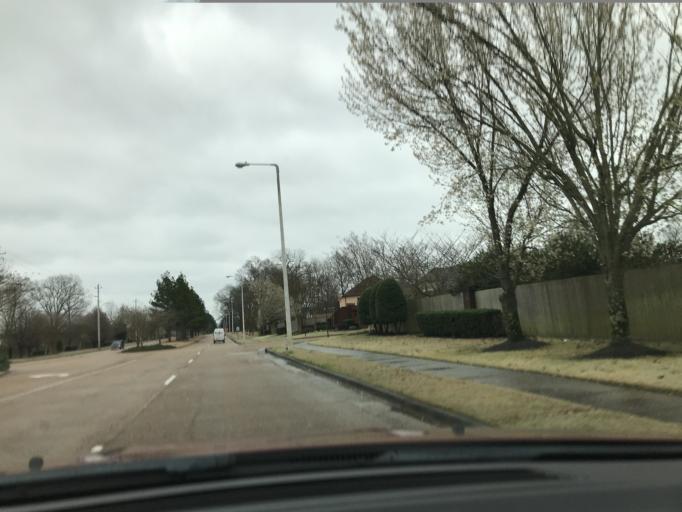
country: US
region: Tennessee
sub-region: Shelby County
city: Collierville
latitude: 35.0856
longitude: -89.7000
